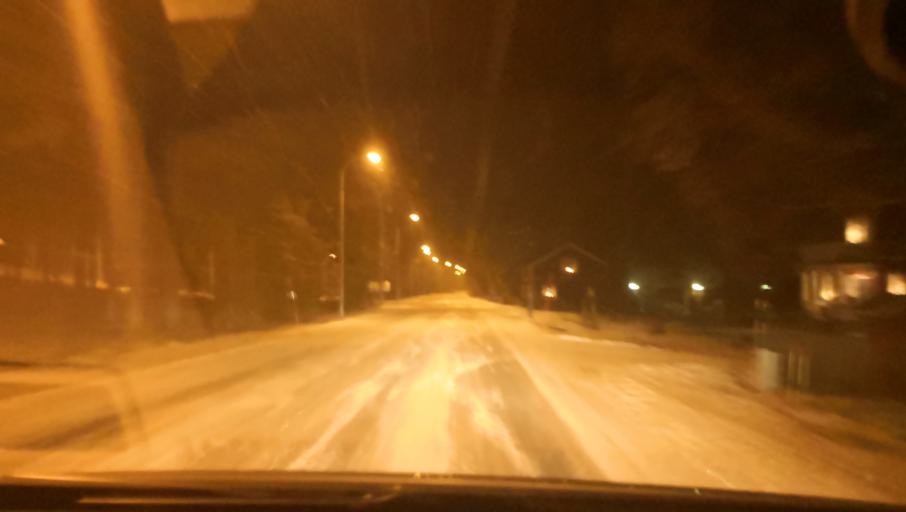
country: SE
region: Uppsala
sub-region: Heby Kommun
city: Tarnsjo
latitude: 60.1486
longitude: 16.9191
